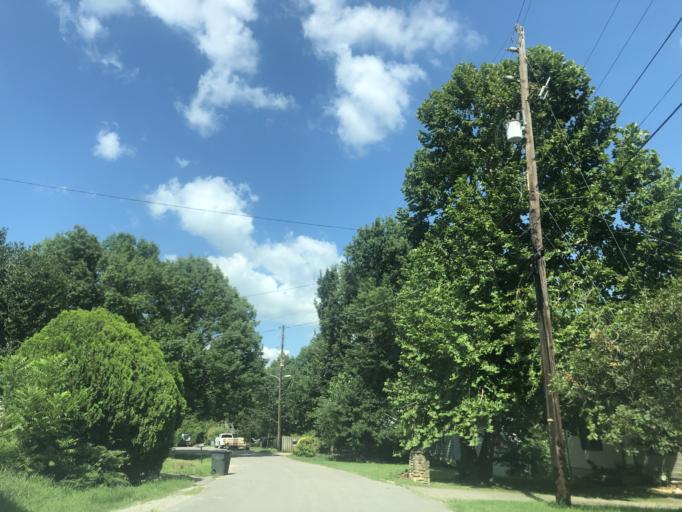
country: US
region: Tennessee
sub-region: Wilson County
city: Green Hill
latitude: 36.2085
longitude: -86.5849
